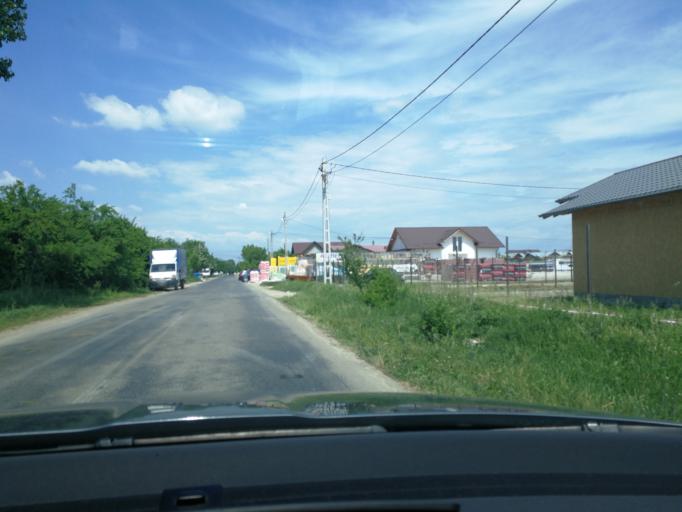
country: RO
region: Prahova
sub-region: Comuna Targsoru Vechi
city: Targsoru Vechi
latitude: 44.8680
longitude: 25.9221
